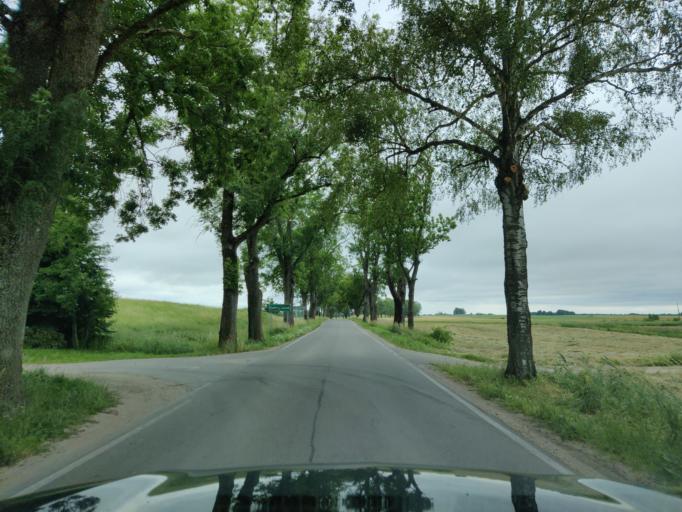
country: PL
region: Warmian-Masurian Voivodeship
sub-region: Powiat mragowski
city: Mikolajki
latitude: 53.8741
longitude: 21.5949
